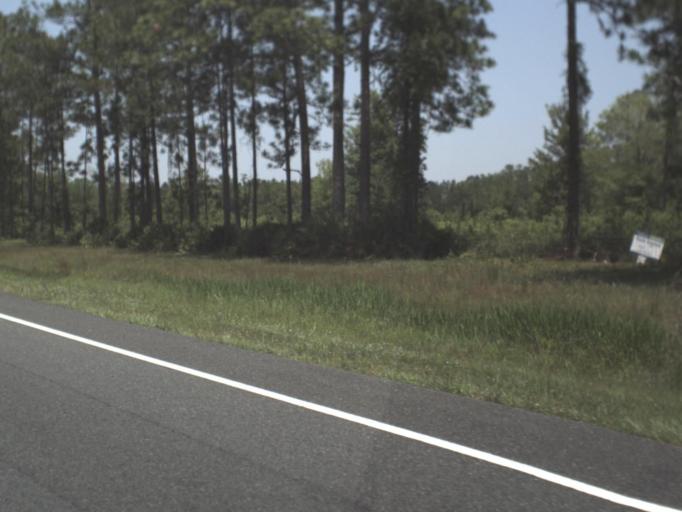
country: US
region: Florida
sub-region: Baker County
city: Macclenny
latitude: 30.2361
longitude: -82.2988
